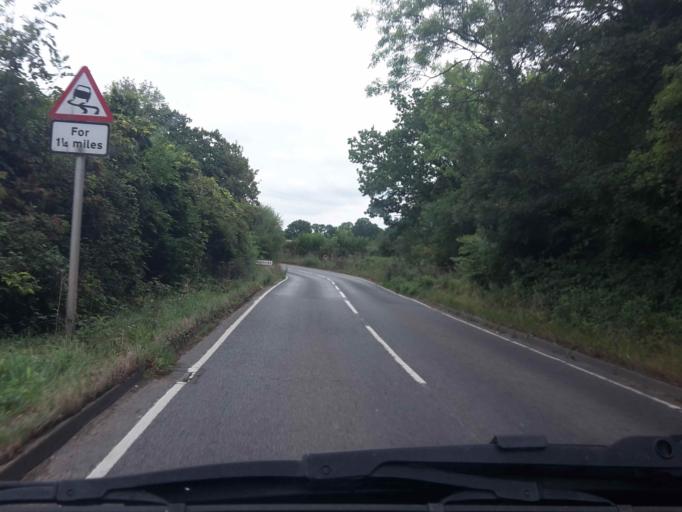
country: GB
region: England
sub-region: Oxfordshire
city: Sonning Common
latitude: 51.4927
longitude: -0.9620
